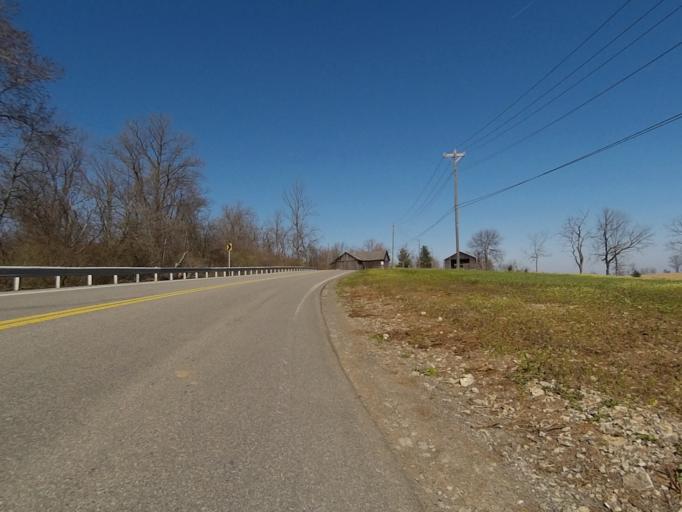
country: US
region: Pennsylvania
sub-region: Centre County
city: Stormstown
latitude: 40.8081
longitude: -77.9971
